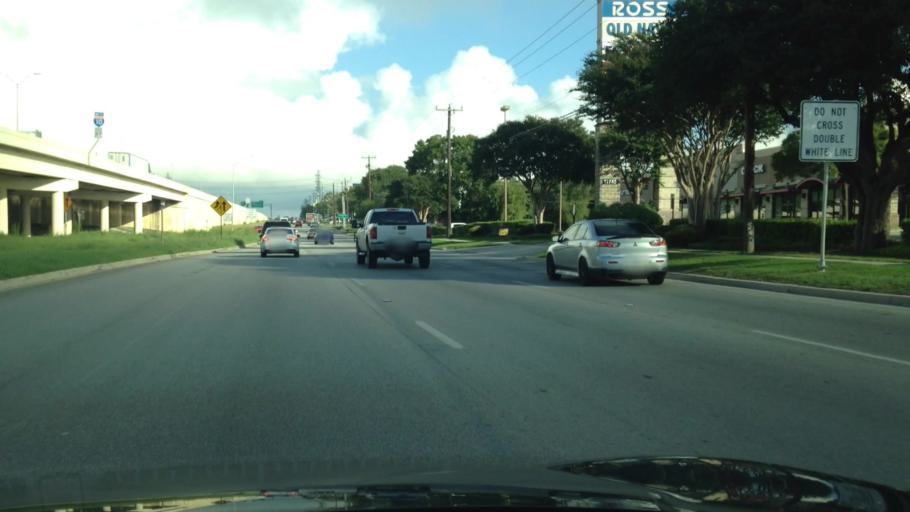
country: US
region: Texas
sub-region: Bexar County
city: Shavano Park
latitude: 29.5498
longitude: -98.5846
